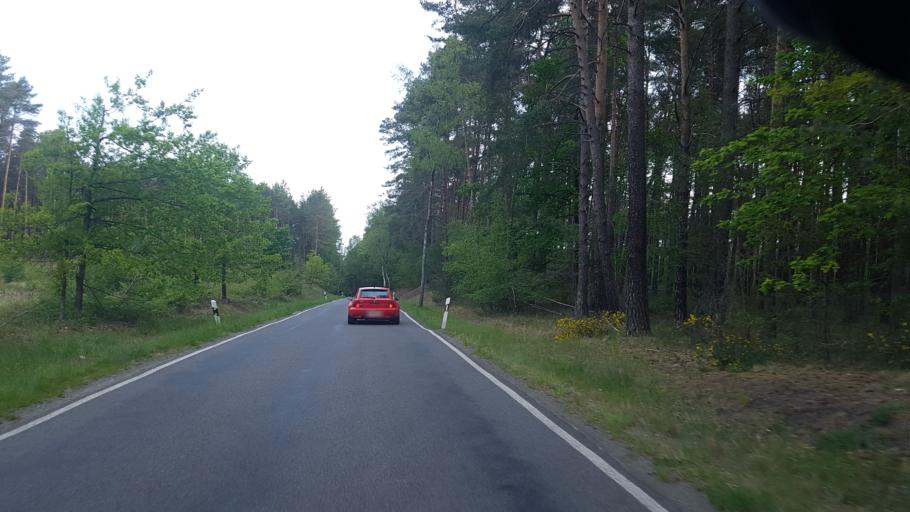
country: DE
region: Brandenburg
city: Baruth
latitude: 51.9970
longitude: 13.4796
